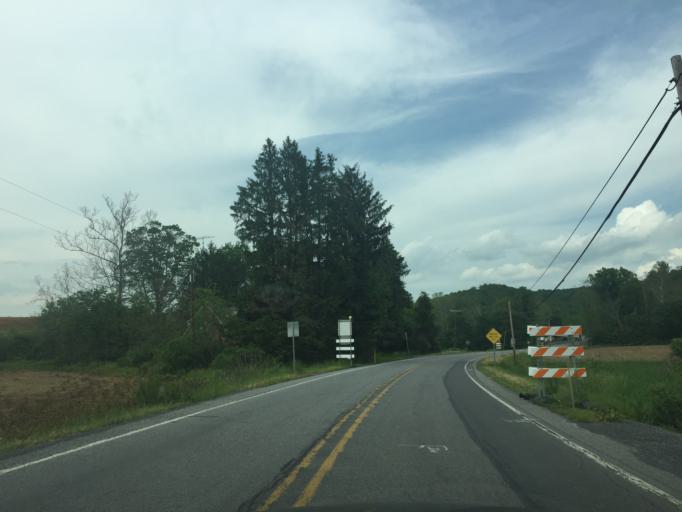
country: US
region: Maryland
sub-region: Washington County
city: Hancock
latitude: 39.8541
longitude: -78.1397
